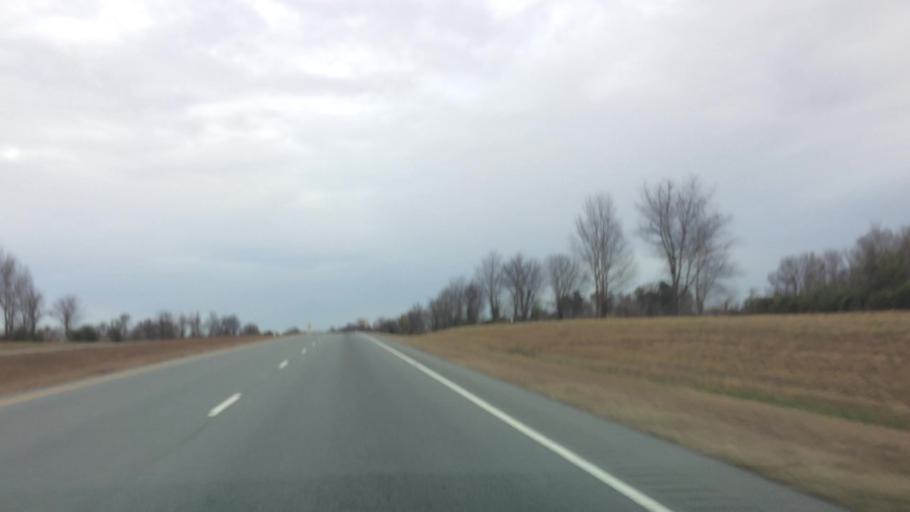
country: US
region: North Carolina
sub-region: Wayne County
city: Mount Olive
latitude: 35.1506
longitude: -78.1194
